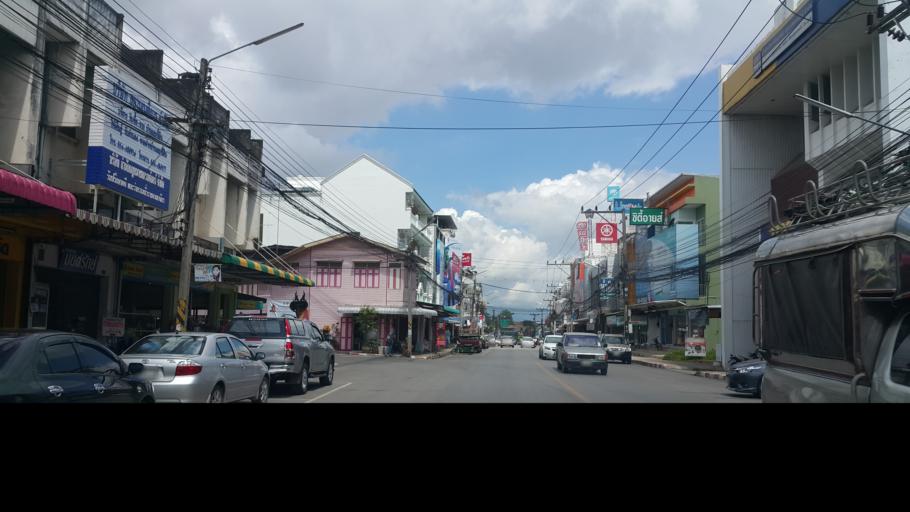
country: TH
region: Phayao
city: Phayao
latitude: 19.1689
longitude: 99.9000
